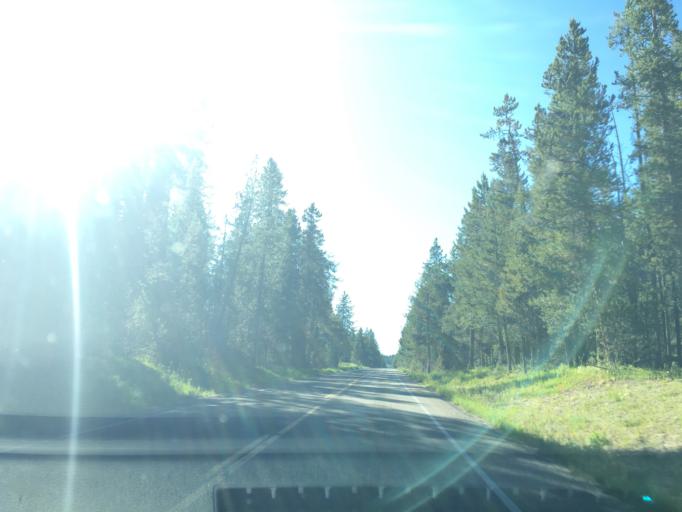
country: US
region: Wyoming
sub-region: Teton County
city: Jackson
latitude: 43.8567
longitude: -110.5256
